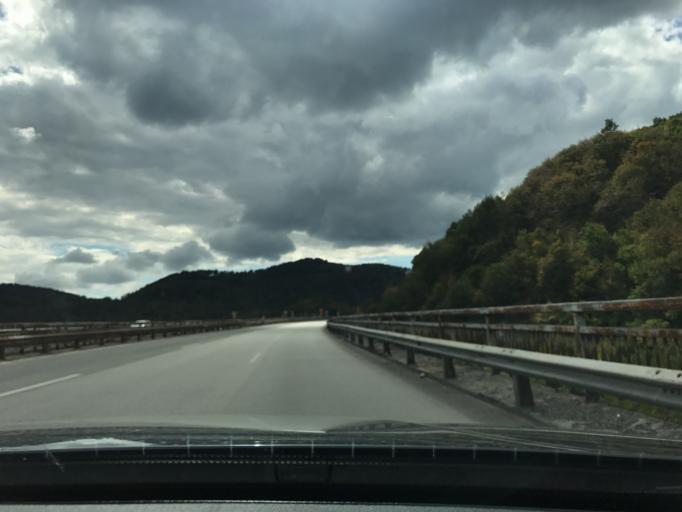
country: BG
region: Sofiya
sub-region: Obshtina Botevgrad
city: Botevgrad
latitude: 42.7982
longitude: 23.8111
